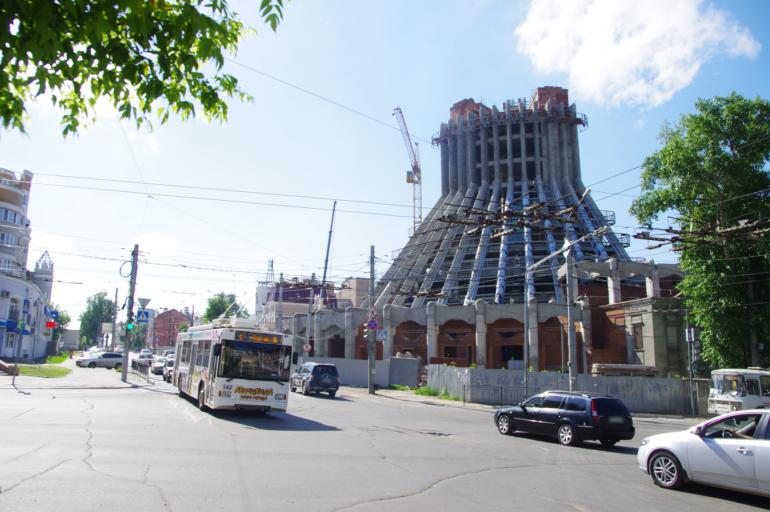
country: RU
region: Kaluga
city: Kaluga
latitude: 54.5137
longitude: 36.2389
